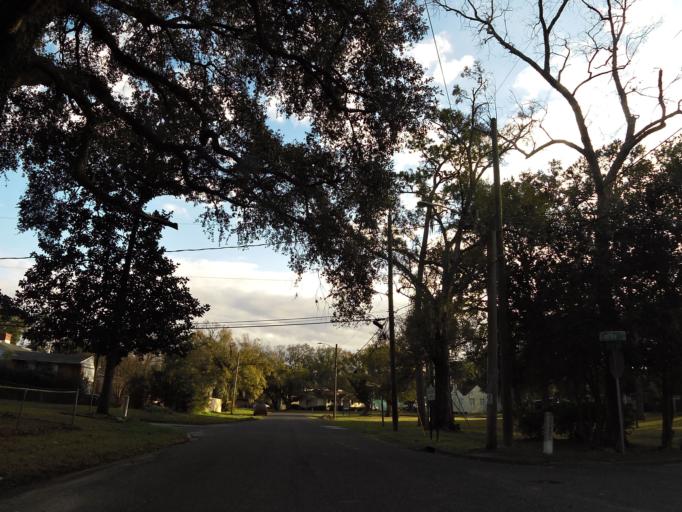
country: US
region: Florida
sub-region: Duval County
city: Jacksonville
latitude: 30.3128
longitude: -81.7095
